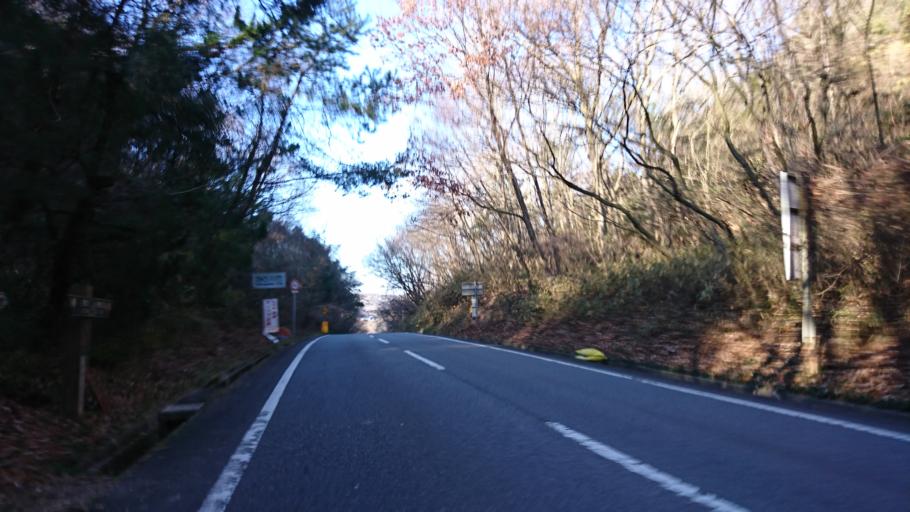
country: JP
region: Hyogo
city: Ono
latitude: 34.8388
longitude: 134.8822
